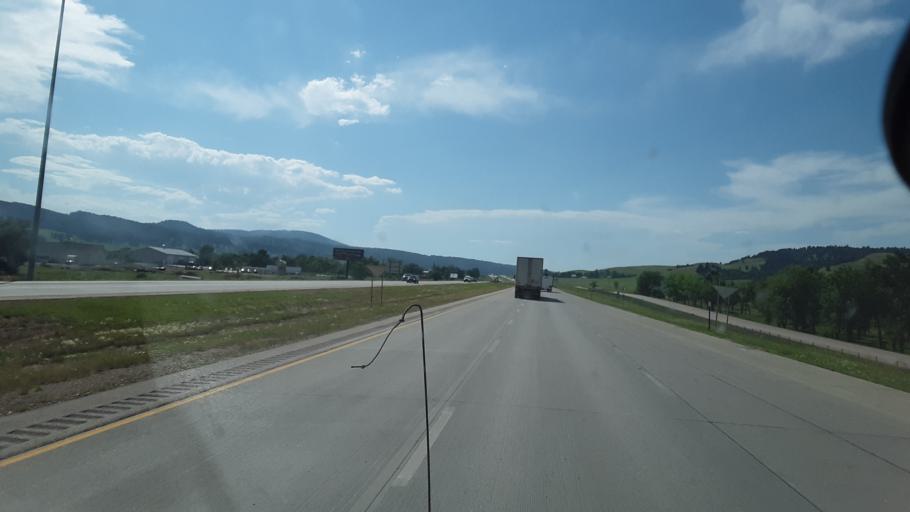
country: US
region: South Dakota
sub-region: Meade County
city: Sturgis
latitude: 44.4204
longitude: -103.5358
